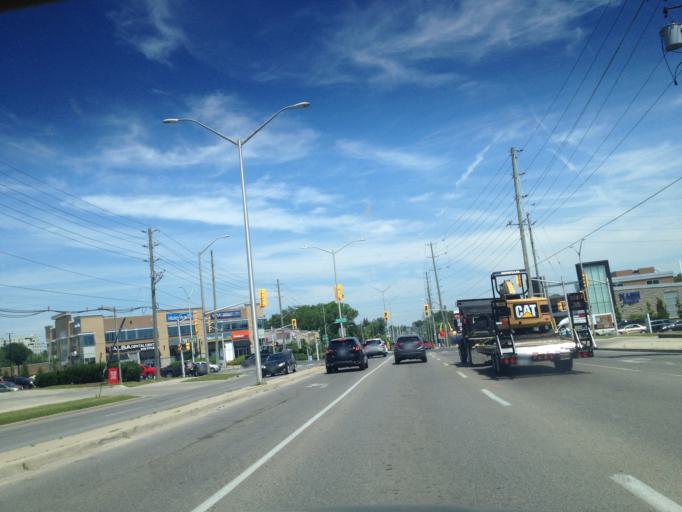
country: CA
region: Ontario
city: London
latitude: 42.9835
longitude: -81.2936
